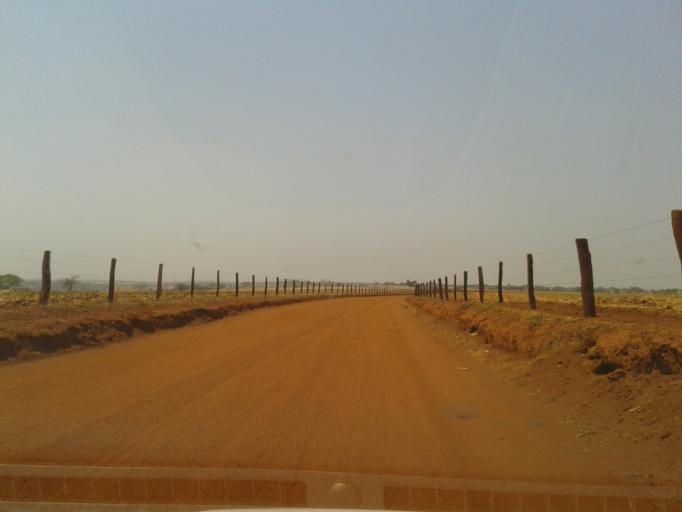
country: BR
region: Minas Gerais
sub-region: Centralina
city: Centralina
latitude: -18.7137
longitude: -49.2254
